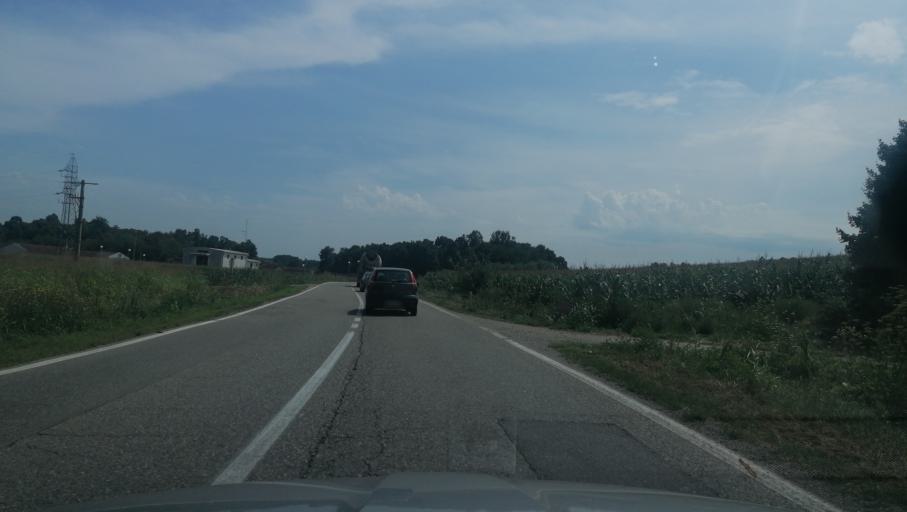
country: BA
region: Republika Srpska
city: Velika Obarska
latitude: 44.7915
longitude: 19.0851
